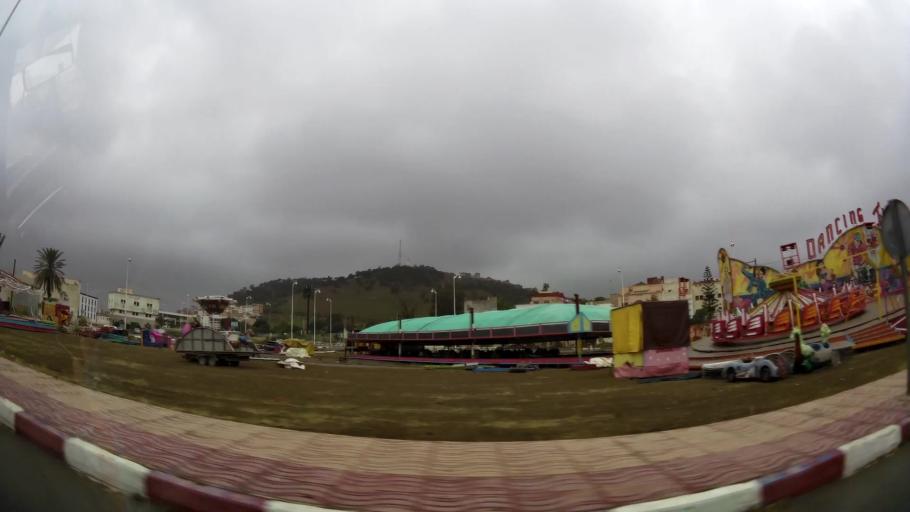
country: MA
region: Oriental
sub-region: Nador
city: Nador
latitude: 35.1865
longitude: -2.9260
